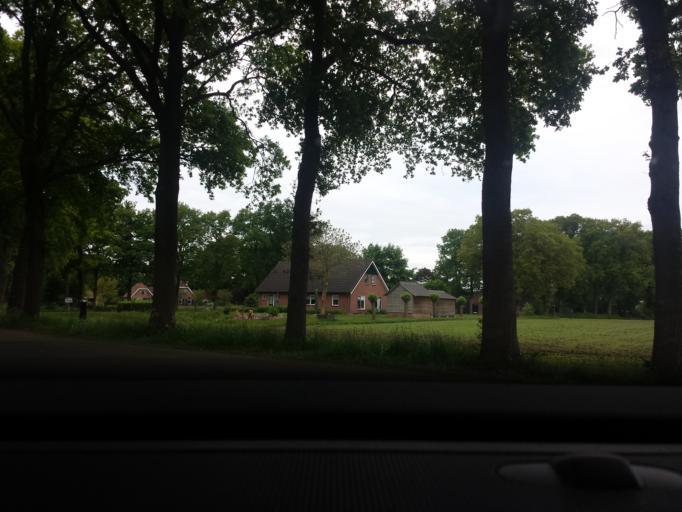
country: NL
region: Gelderland
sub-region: Oost Gelre
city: Lichtenvoorde
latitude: 52.0426
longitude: 6.5828
